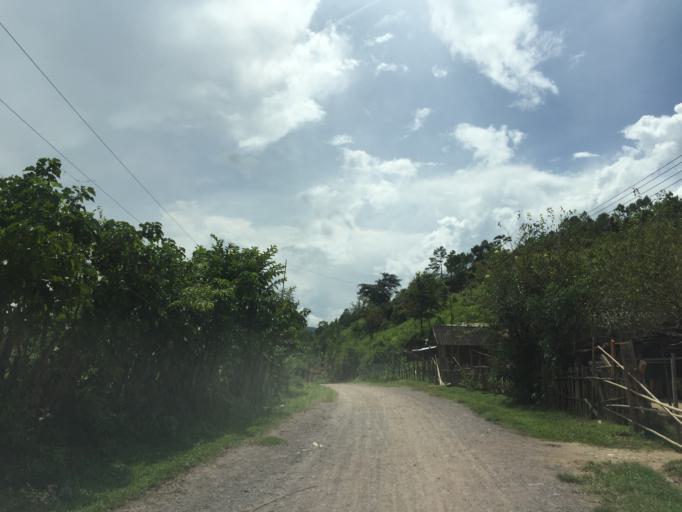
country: LA
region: Xiangkhoang
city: Muang Phonsavan
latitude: 19.3411
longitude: 103.5430
